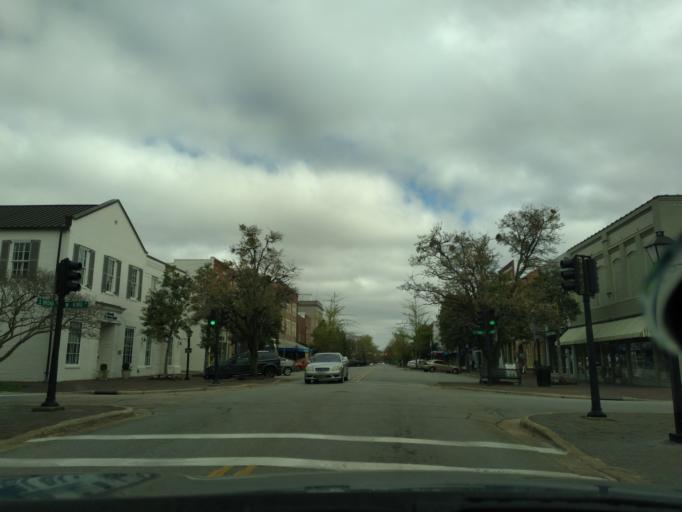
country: US
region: North Carolina
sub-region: Chowan County
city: Edenton
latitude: 36.0578
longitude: -76.6092
